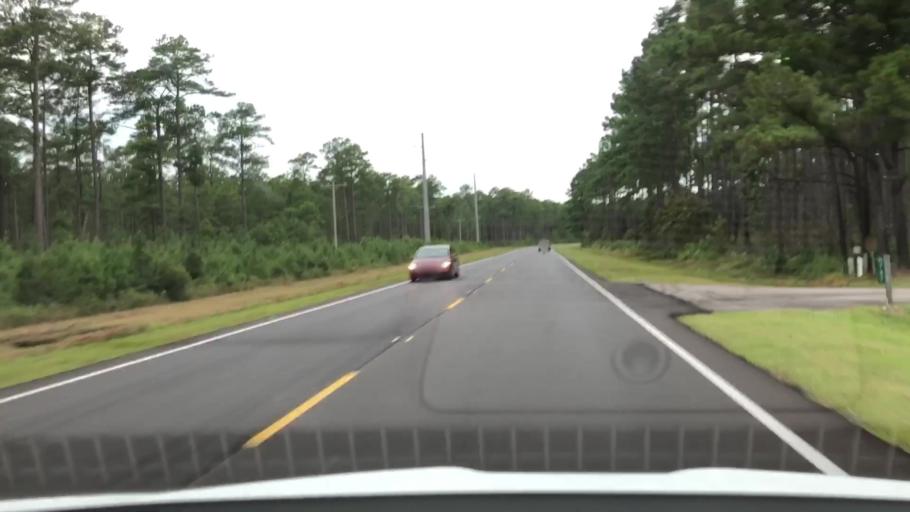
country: US
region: North Carolina
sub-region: Jones County
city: Maysville
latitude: 34.8157
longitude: -77.1433
